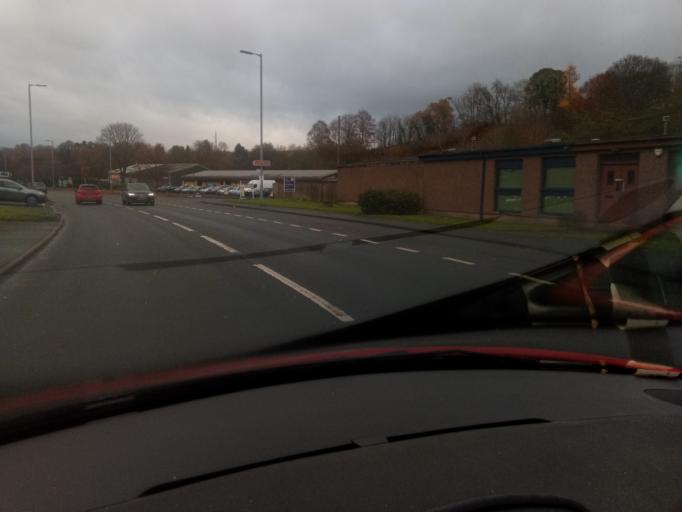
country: GB
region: Scotland
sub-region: The Scottish Borders
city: Jedburgh
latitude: 55.4877
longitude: -2.5453
